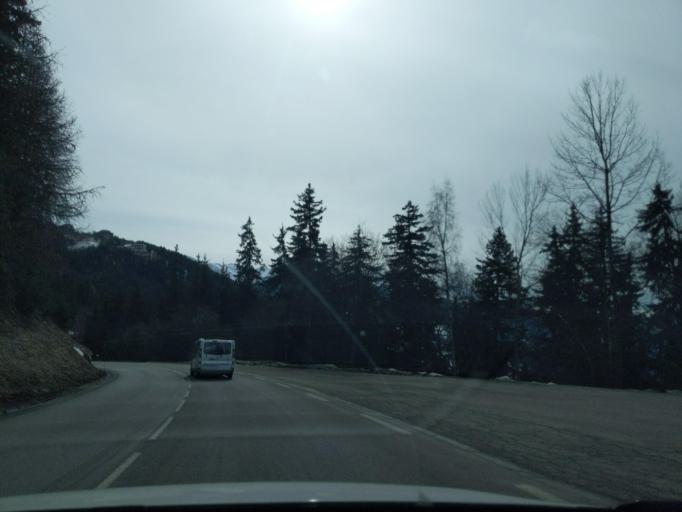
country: FR
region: Rhone-Alpes
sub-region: Departement de la Savoie
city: Bourg-Saint-Maurice
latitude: 45.5894
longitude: 6.7851
